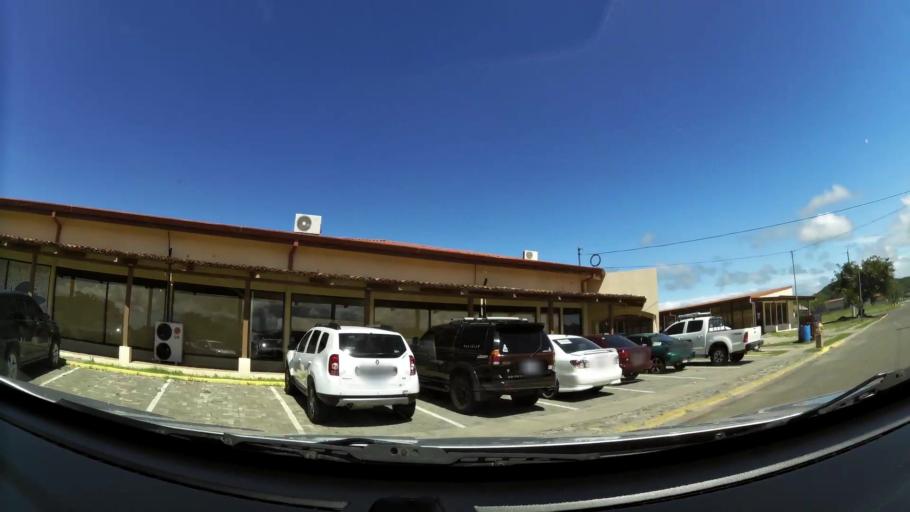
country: CR
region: Guanacaste
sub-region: Canton de Canas
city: Canas
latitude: 10.4328
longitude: -85.0854
